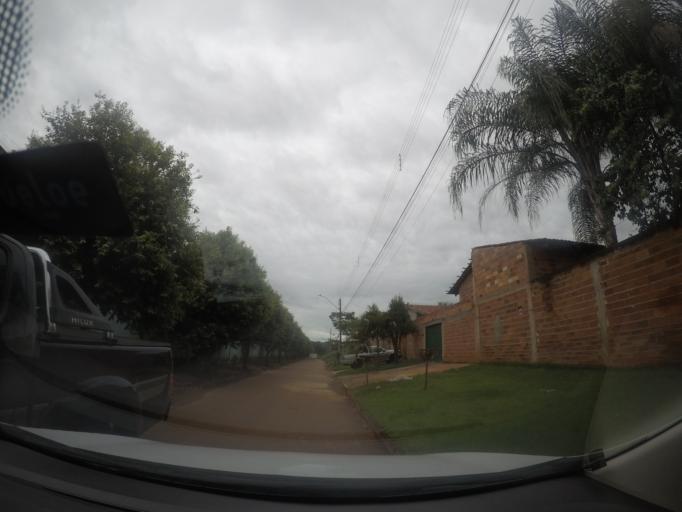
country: BR
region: Goias
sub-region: Goiania
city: Goiania
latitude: -16.6311
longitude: -49.3058
